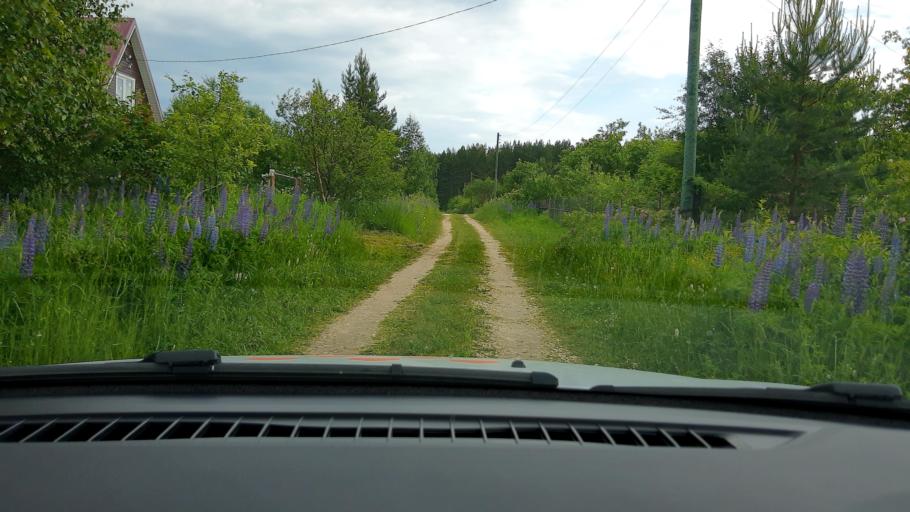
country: RU
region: Nizjnij Novgorod
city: Surovatikha
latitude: 55.8683
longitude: 43.9646
